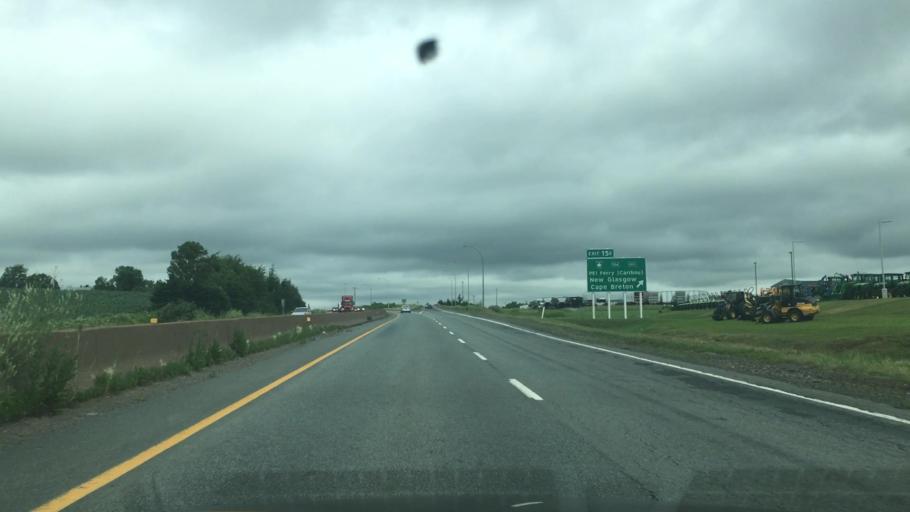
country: CA
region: Nova Scotia
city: Truro
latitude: 45.3826
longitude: -63.3216
